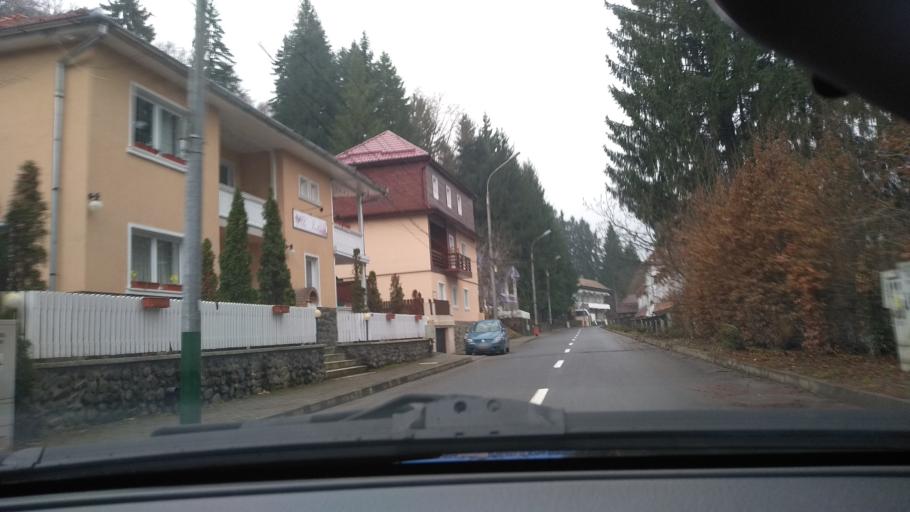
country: RO
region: Mures
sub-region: Oras Sovata
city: Sovata
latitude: 46.5984
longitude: 25.0854
